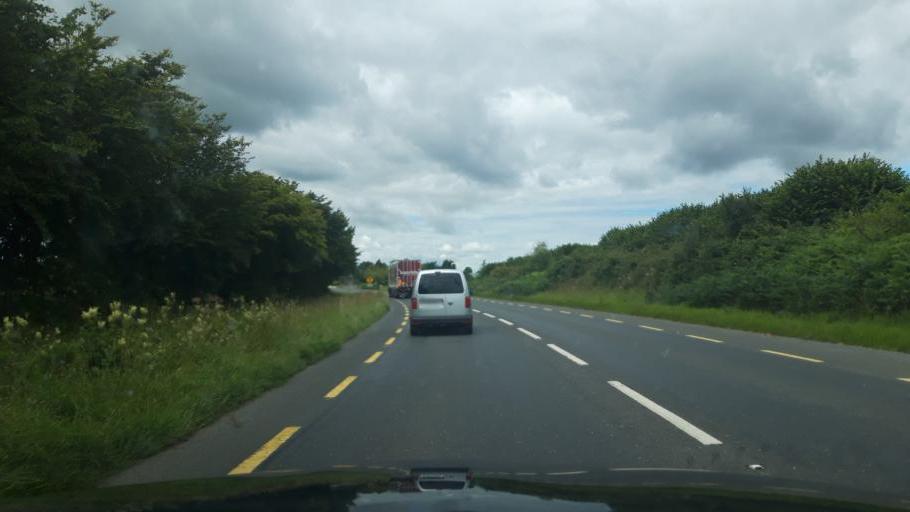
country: IE
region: Munster
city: Carrick-on-Suir
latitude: 52.3931
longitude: -7.5136
